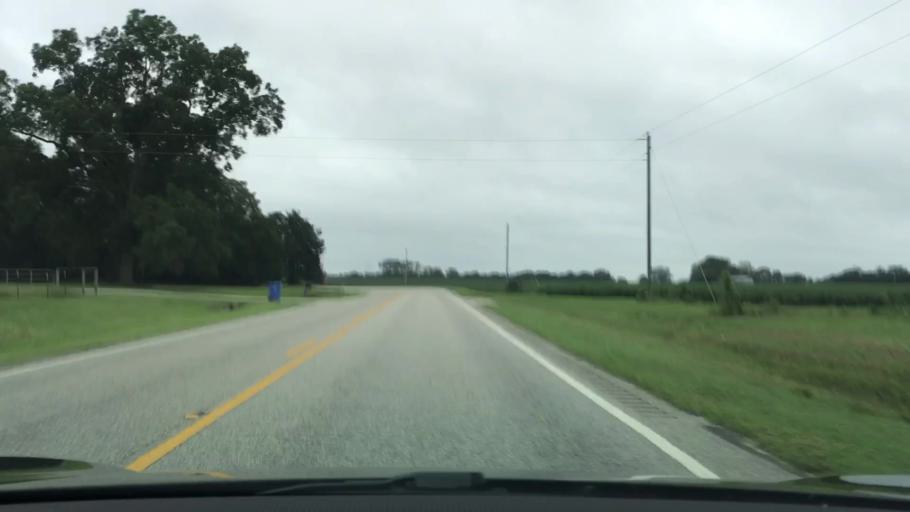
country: US
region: Alabama
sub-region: Coffee County
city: Elba
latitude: 31.3332
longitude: -86.1320
